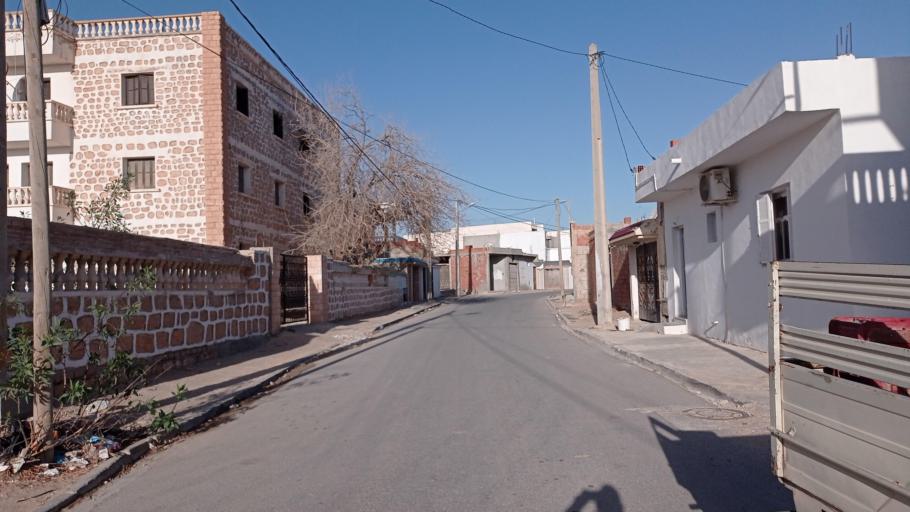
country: TN
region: Qabis
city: Gabes
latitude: 33.8554
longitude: 10.1196
